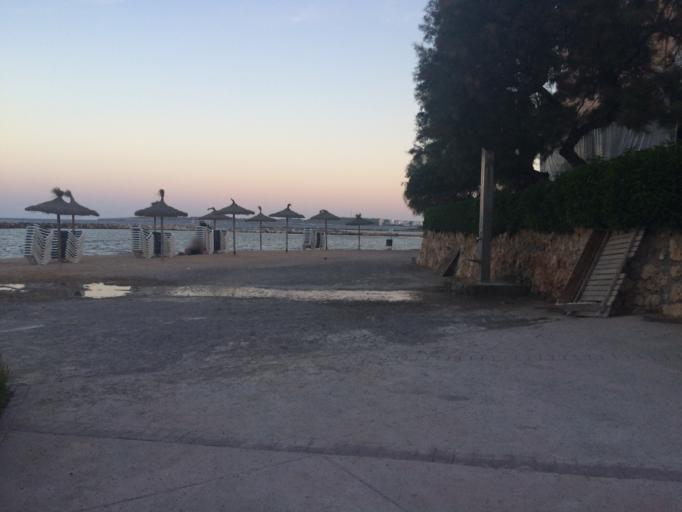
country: ES
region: Balearic Islands
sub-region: Illes Balears
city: Son Servera
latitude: 39.6123
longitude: 3.3917
